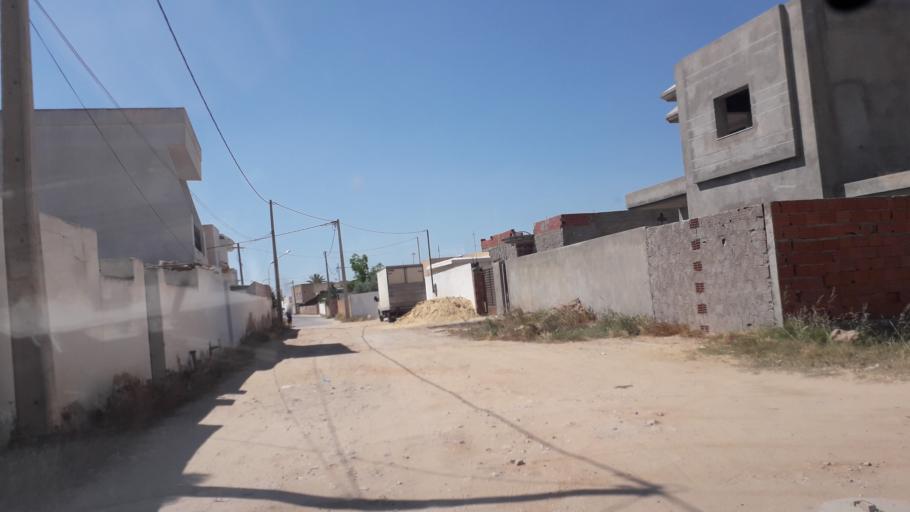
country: TN
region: Safaqis
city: Al Qarmadah
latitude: 34.8169
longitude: 10.7649
